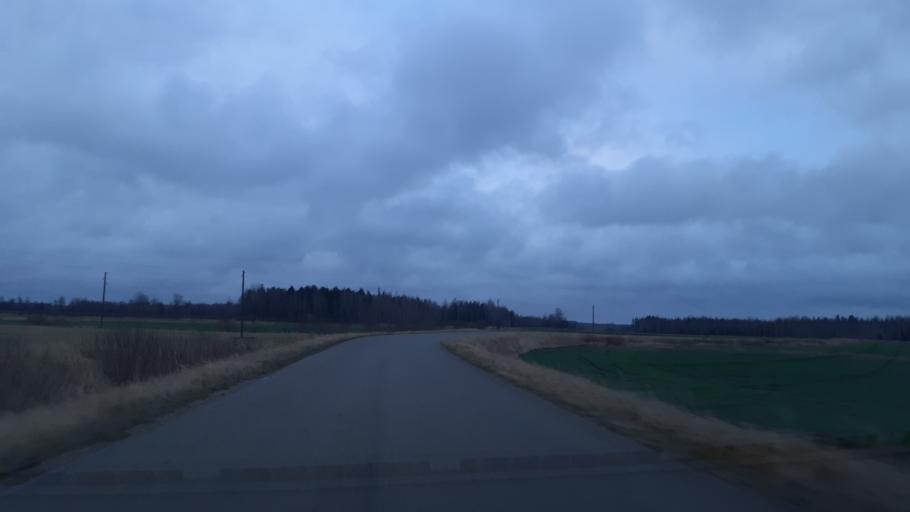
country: LV
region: Kuldigas Rajons
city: Kuldiga
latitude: 57.0407
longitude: 22.1452
